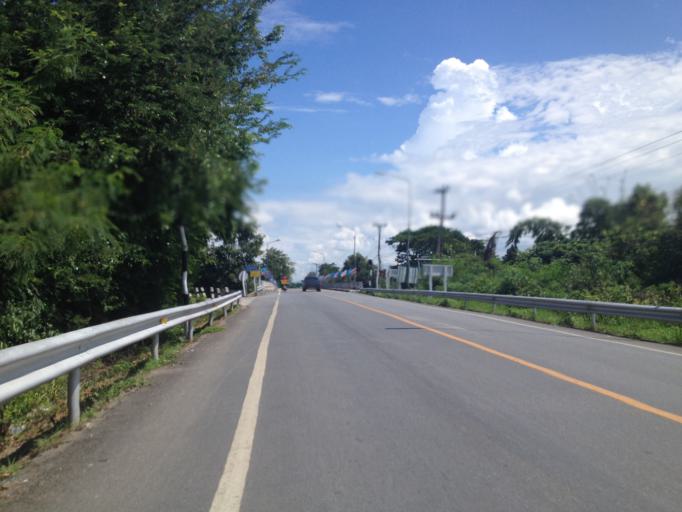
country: TH
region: Lamphun
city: Lamphun
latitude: 18.5999
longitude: 98.9649
